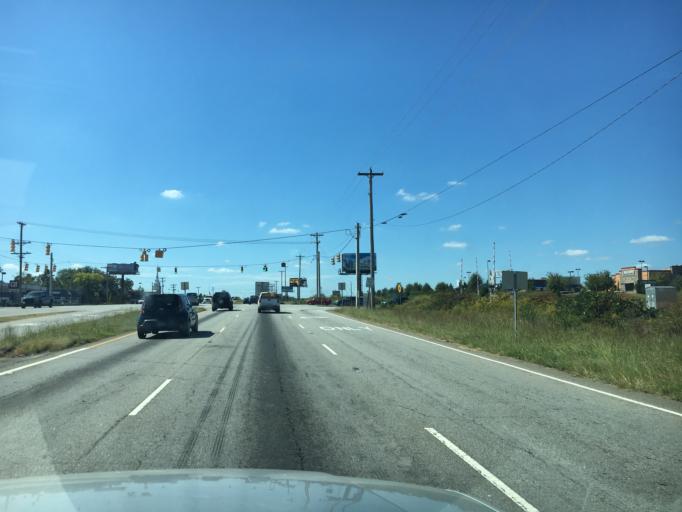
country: US
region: South Carolina
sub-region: Pickens County
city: Easley
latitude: 34.8264
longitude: -82.5444
